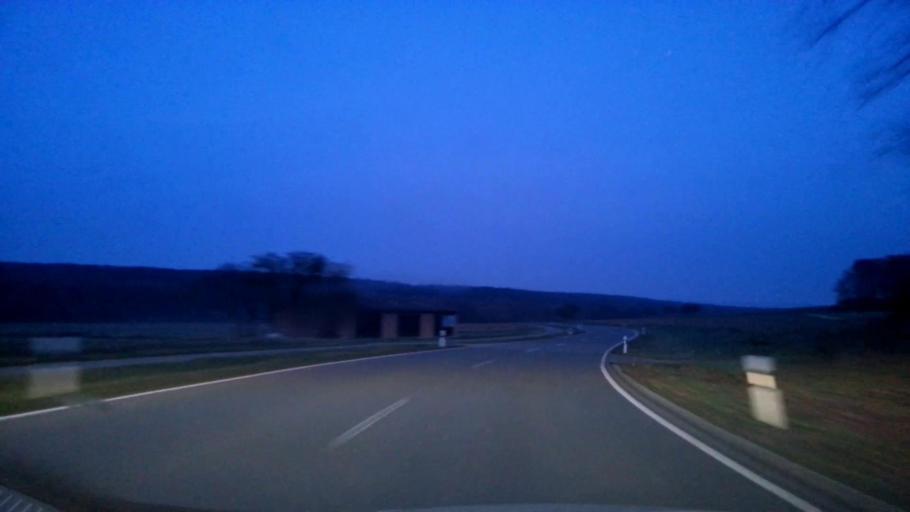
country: DE
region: Bavaria
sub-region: Upper Franconia
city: Pettstadt
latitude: 49.8460
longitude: 10.9005
